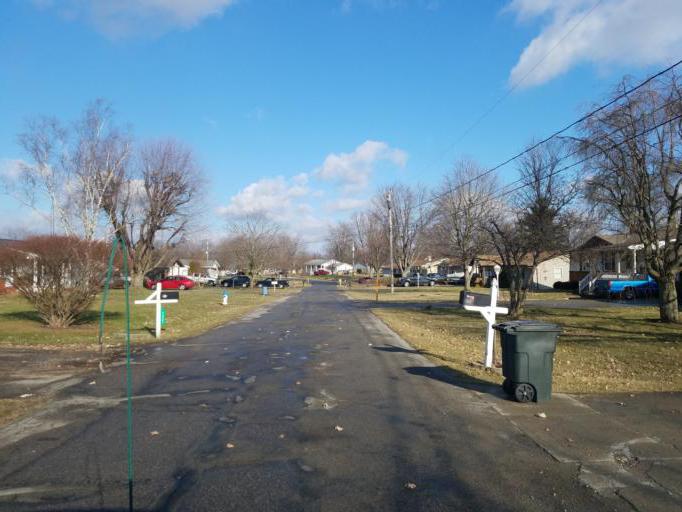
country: US
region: Ohio
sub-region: Marion County
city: Marion
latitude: 40.5648
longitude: -83.1558
